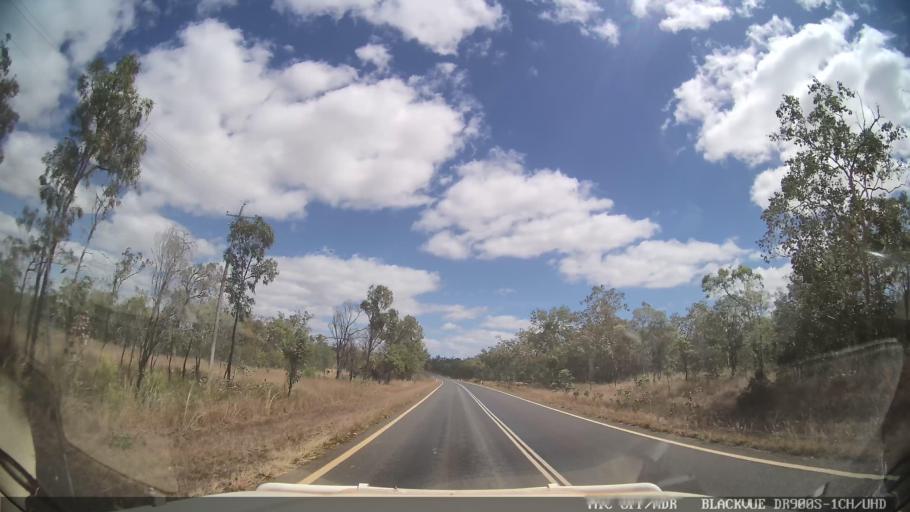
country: AU
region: Queensland
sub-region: Tablelands
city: Ravenshoe
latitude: -17.9062
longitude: 144.8852
